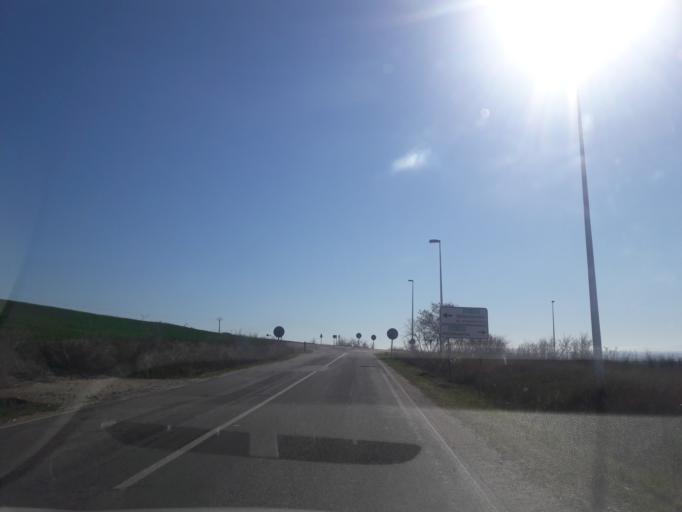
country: ES
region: Castille and Leon
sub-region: Provincia de Salamanca
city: Macotera
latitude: 40.8332
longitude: -5.2776
